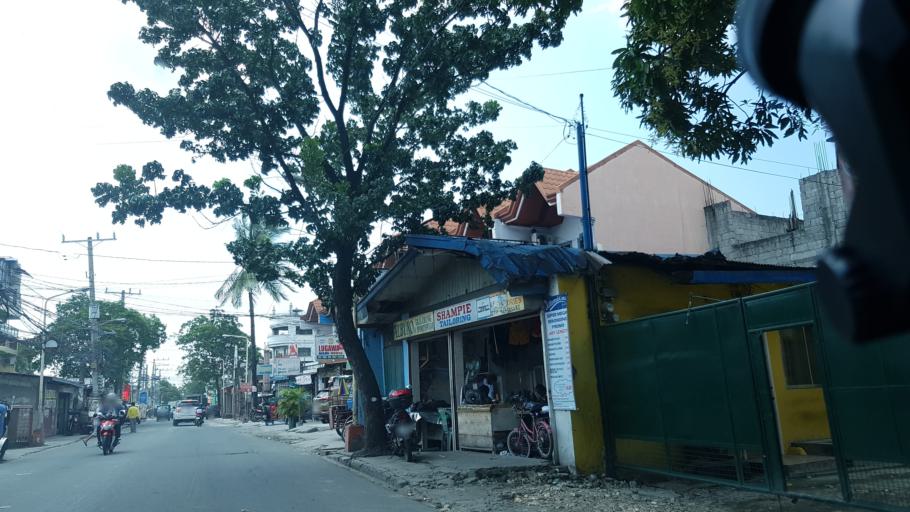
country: PH
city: Sambayanihan People's Village
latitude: 14.4624
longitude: 120.9909
